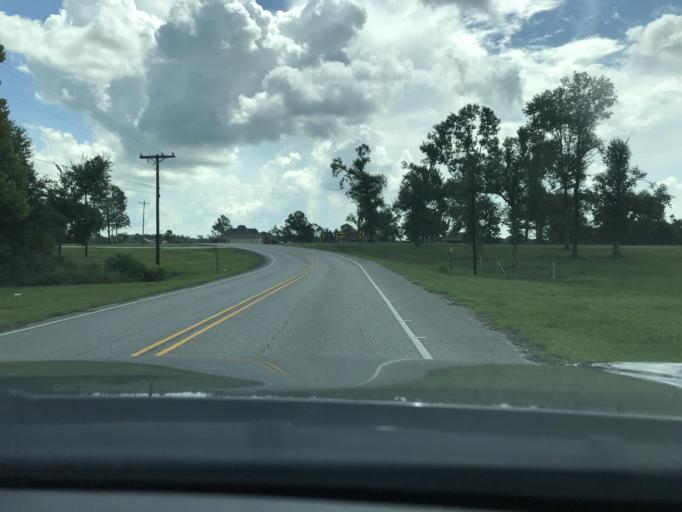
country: US
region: Louisiana
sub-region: Calcasieu Parish
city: Moss Bluff
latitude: 30.3398
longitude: -93.2463
